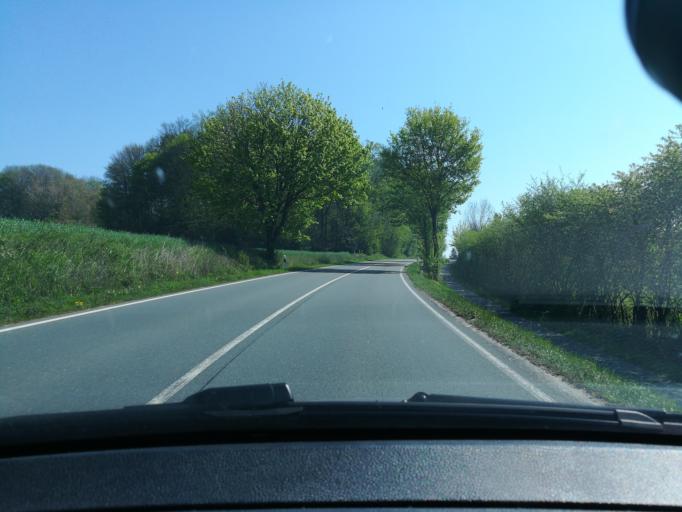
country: DE
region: North Rhine-Westphalia
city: Borgholzhausen
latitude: 52.0920
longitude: 8.2814
